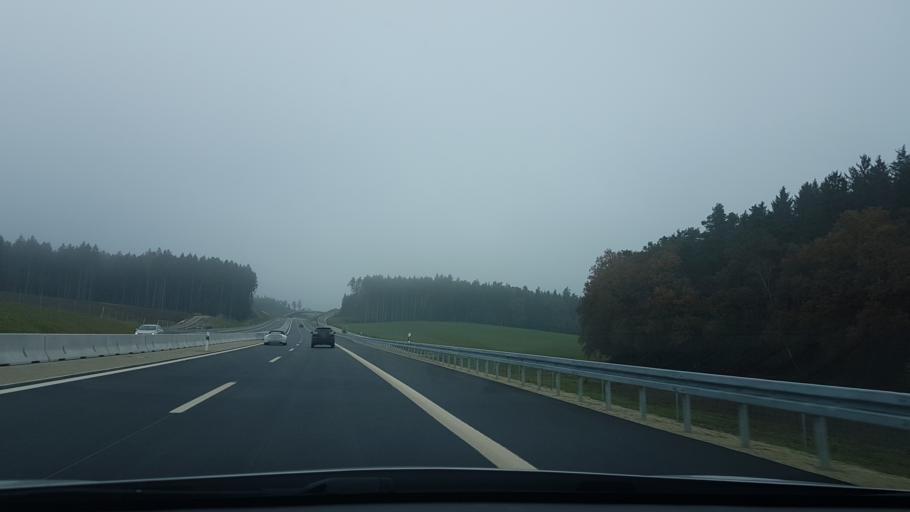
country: DE
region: Bavaria
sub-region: Lower Bavaria
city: Buch
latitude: 48.6468
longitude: 12.1972
